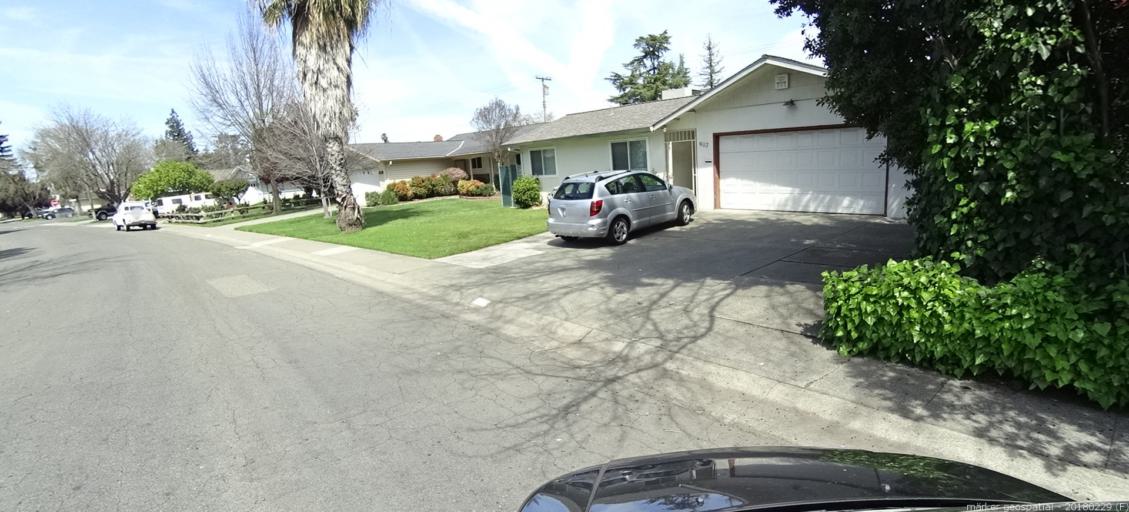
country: US
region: California
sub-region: Sacramento County
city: Rosemont
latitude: 38.5511
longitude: -121.3639
